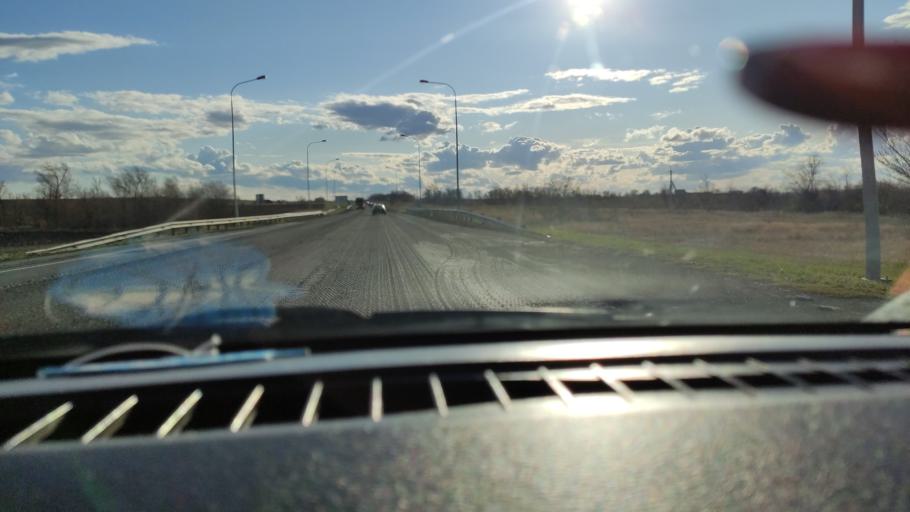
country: RU
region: Saratov
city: Yelshanka
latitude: 51.7931
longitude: 46.1602
